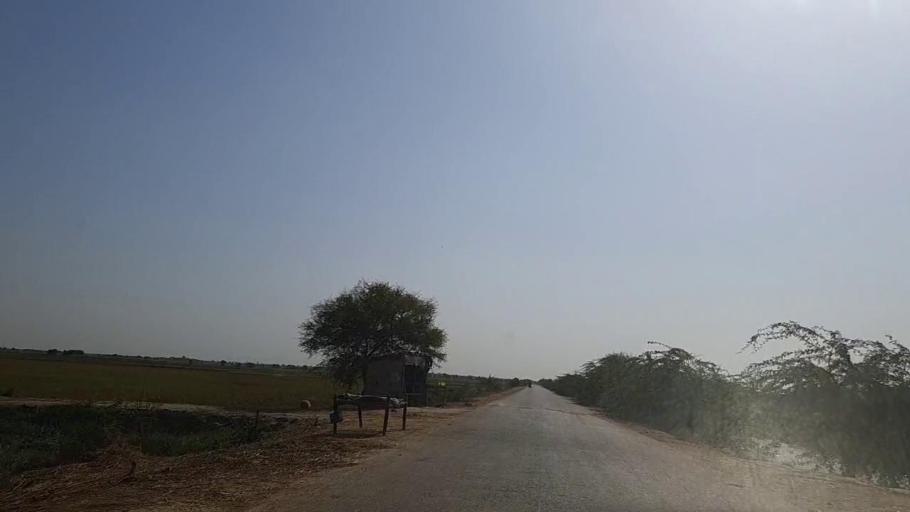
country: PK
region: Sindh
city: Mirpur Batoro
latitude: 24.5914
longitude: 68.2921
